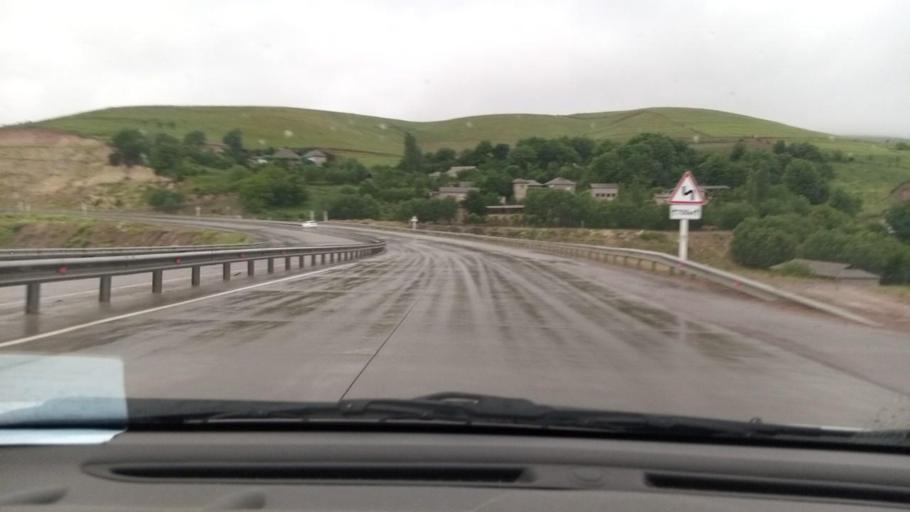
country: UZ
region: Toshkent
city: Angren
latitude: 41.0675
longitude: 70.2231
